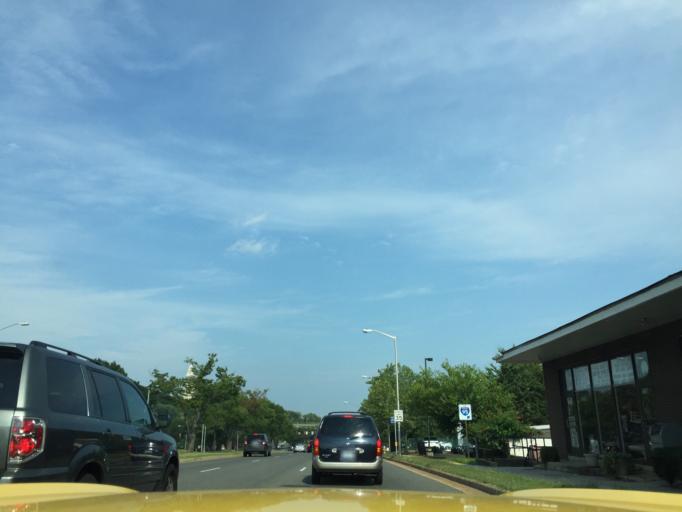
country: US
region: Virginia
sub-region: Fairfax County
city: Huntington
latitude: 38.8069
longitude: -77.0781
